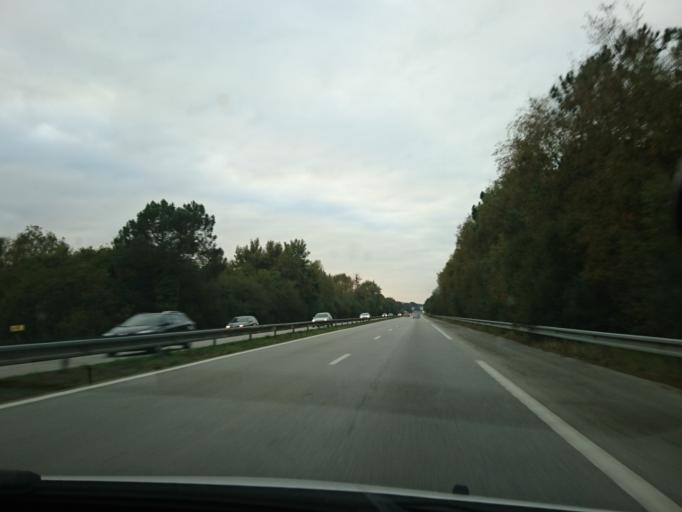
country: FR
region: Brittany
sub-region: Departement du Morbihan
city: Kervignac
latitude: 47.7868
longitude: -3.2294
